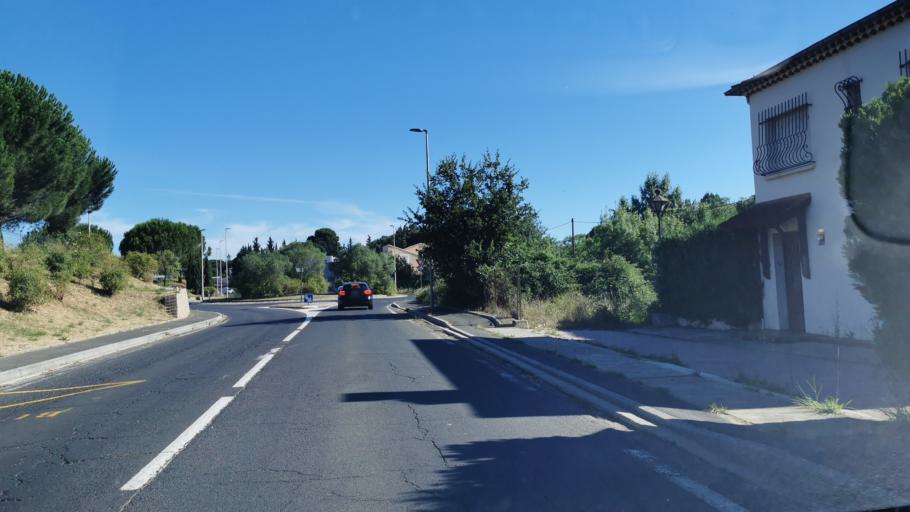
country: FR
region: Languedoc-Roussillon
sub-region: Departement de l'Herault
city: Beziers
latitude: 43.3603
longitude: 3.2125
